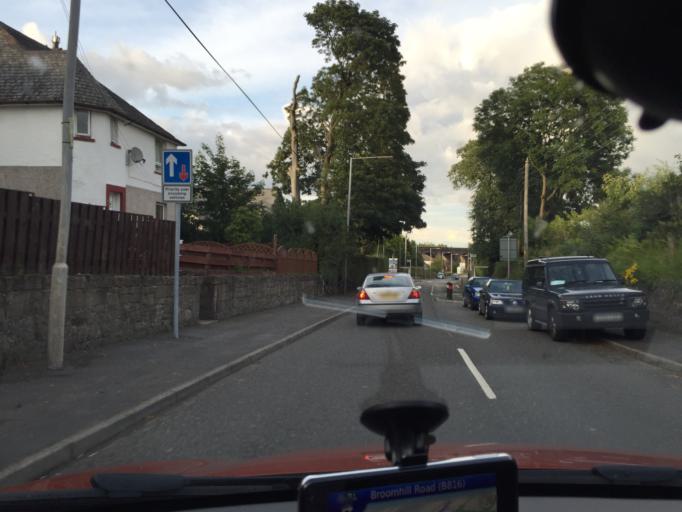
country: GB
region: Scotland
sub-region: North Lanarkshire
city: Cumbernauld
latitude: 55.9793
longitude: -3.9481
